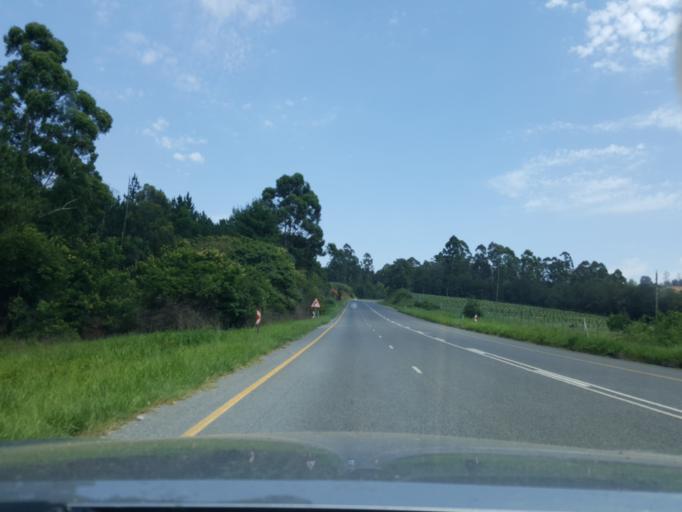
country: ZA
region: Mpumalanga
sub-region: Ehlanzeni District
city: White River
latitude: -25.1490
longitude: 31.0042
